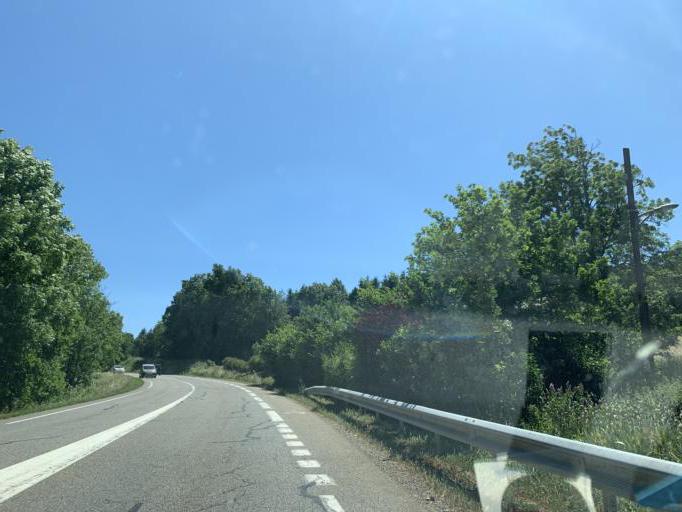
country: FR
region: Provence-Alpes-Cote d'Azur
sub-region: Departement des Hautes-Alpes
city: Gap
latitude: 44.6198
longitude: 6.1346
